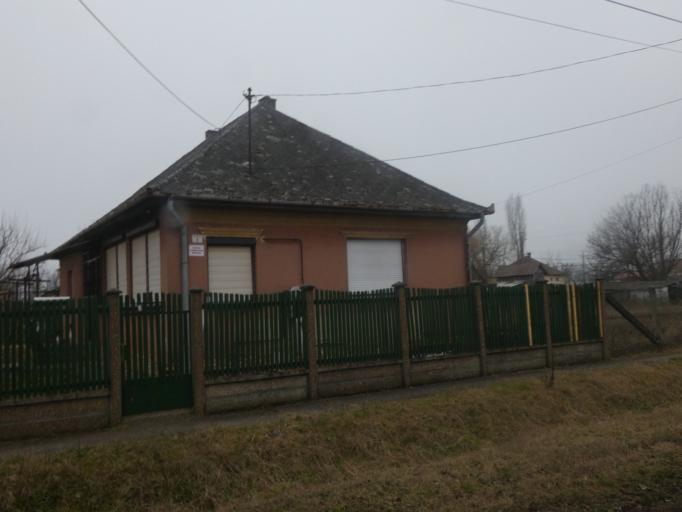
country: HU
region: Pest
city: Tapiogyorgye
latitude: 47.3258
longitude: 19.9514
